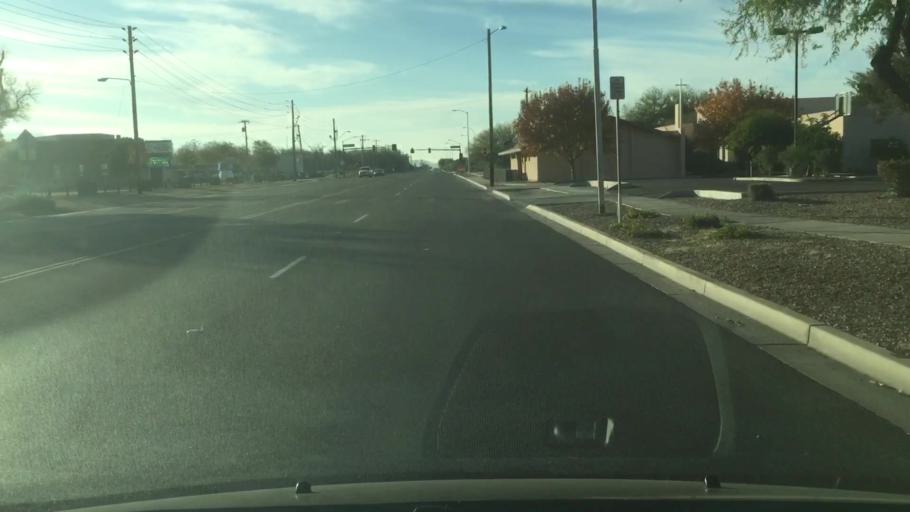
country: US
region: Arizona
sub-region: Maricopa County
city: Laveen
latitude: 33.3631
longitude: -112.1669
